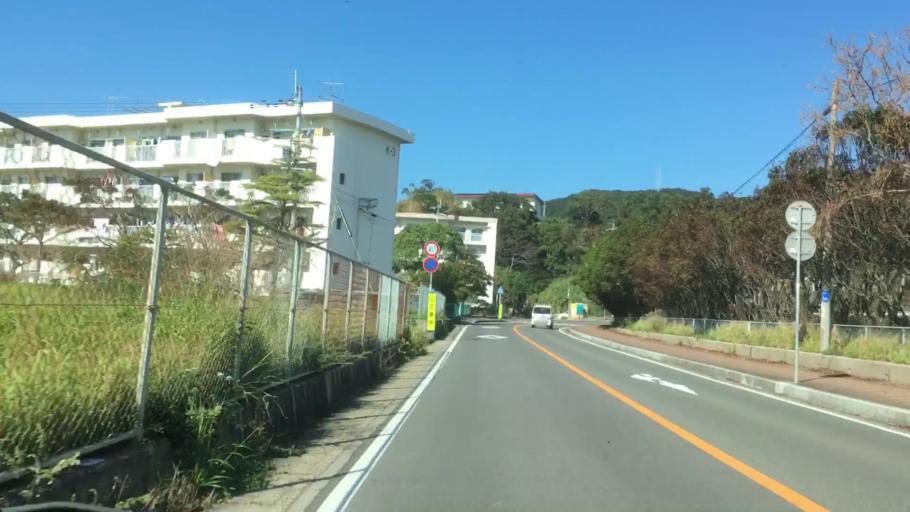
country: JP
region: Nagasaki
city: Sasebo
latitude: 33.0383
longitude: 129.6250
